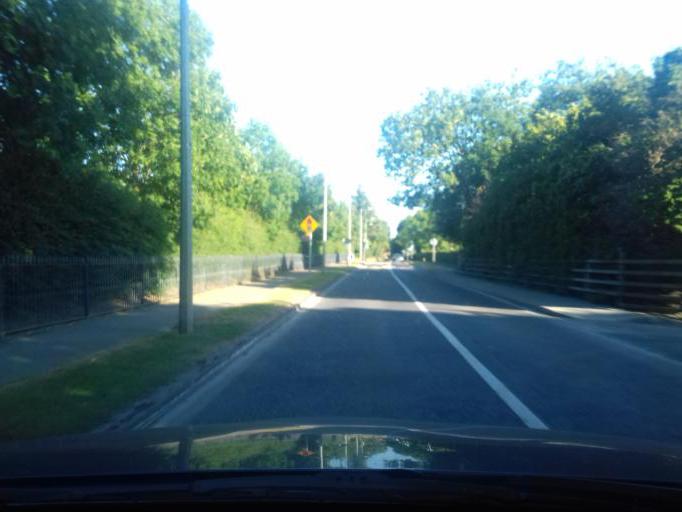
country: IE
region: Leinster
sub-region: Fingal County
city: Blanchardstown
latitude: 53.4320
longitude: -6.3770
